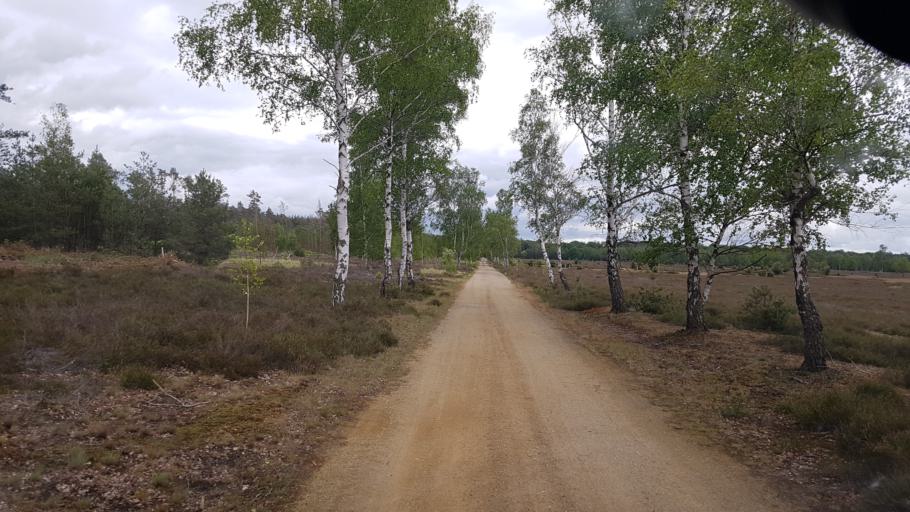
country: DE
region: Brandenburg
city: Hohenleipisch
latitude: 51.5370
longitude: 13.5371
